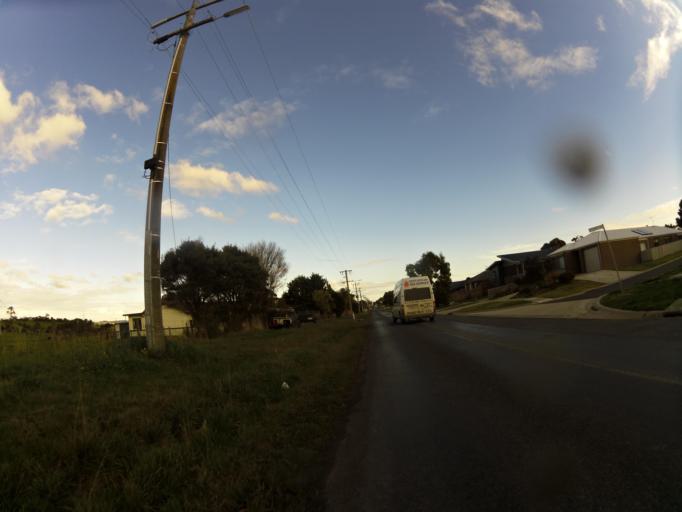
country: AU
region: Victoria
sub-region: Bass Coast
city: North Wonthaggi
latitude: -38.5592
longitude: 145.5483
